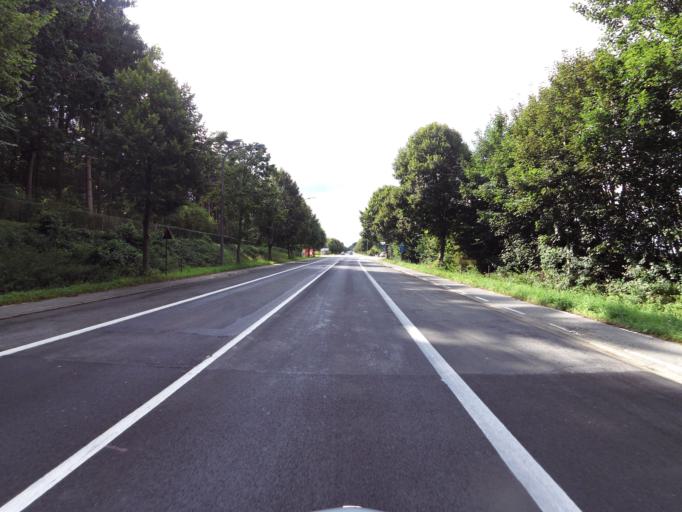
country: BE
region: Flanders
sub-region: Provincie Oost-Vlaanderen
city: Ronse
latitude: 50.7635
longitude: 3.5554
